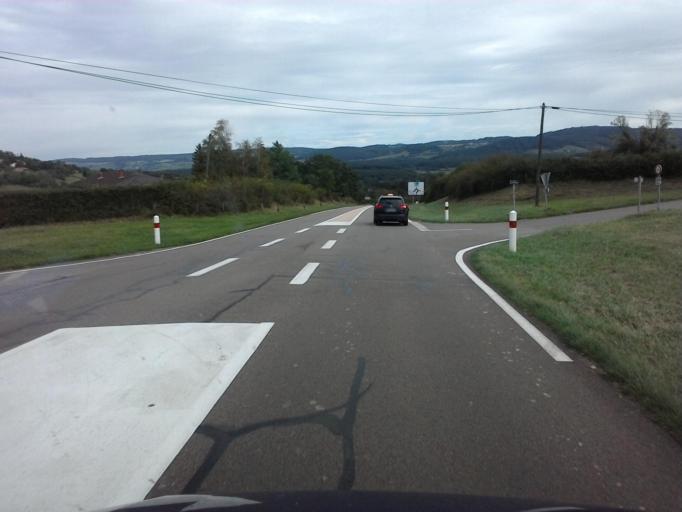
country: FR
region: Bourgogne
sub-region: Departement de Saone-et-Loire
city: Cluny
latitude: 46.4405
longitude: 4.6525
